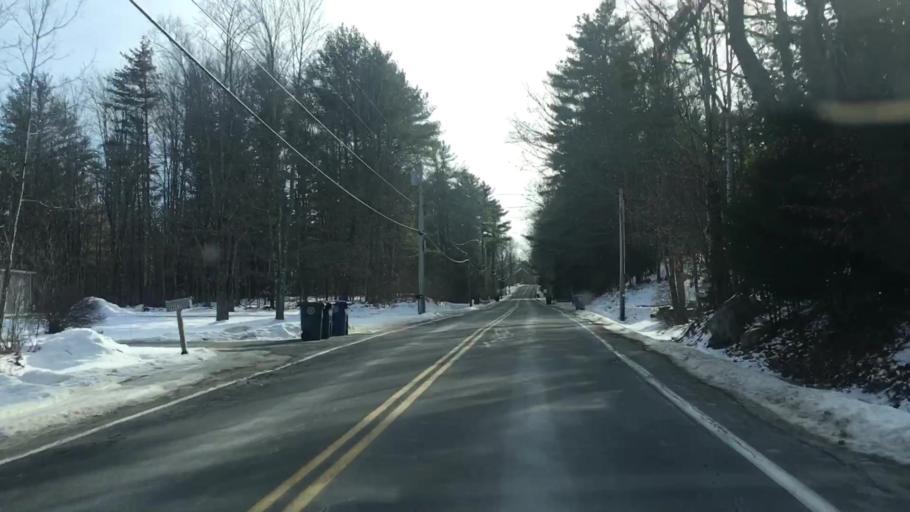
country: US
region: Maine
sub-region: Cumberland County
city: Westbrook
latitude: 43.7250
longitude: -70.3572
